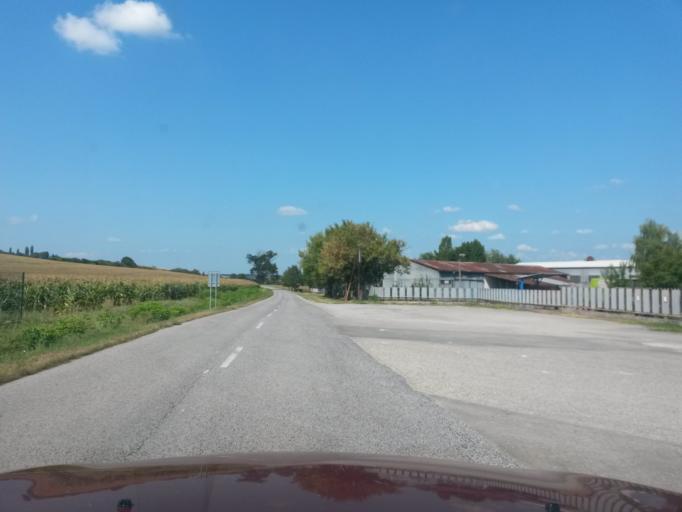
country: SK
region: Kosicky
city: Moldava nad Bodvou
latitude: 48.5338
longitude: 21.0887
